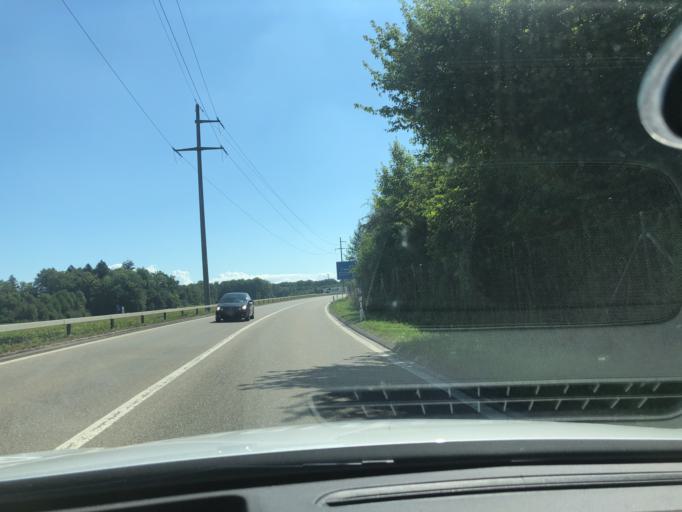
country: CH
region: Thurgau
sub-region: Kreuzlingen District
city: Tagerwilen
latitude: 47.6344
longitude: 9.1484
